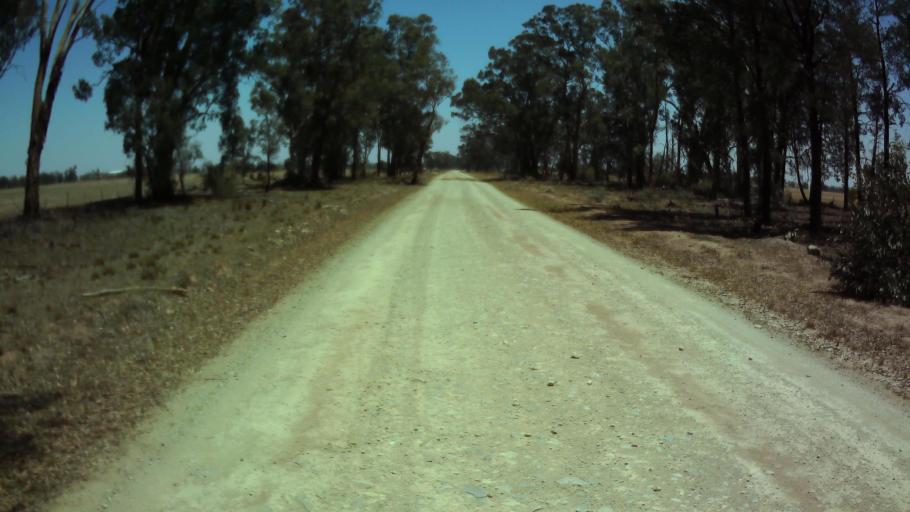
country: AU
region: New South Wales
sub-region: Weddin
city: Grenfell
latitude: -34.0281
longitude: 147.8735
